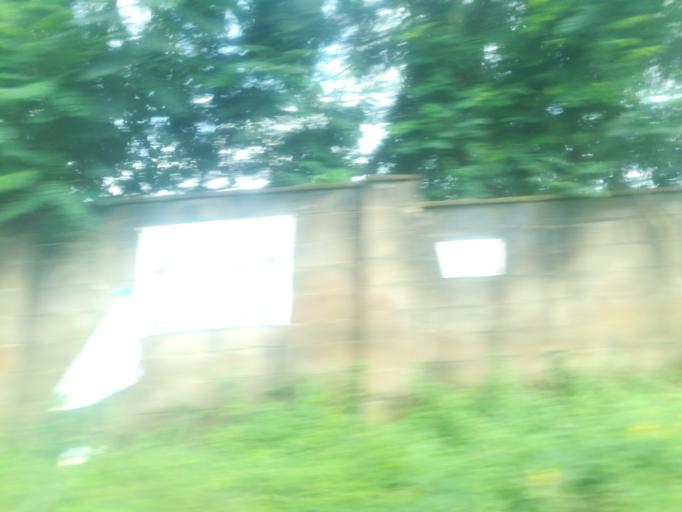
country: NG
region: Oyo
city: Ibadan
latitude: 7.3756
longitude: 3.8360
